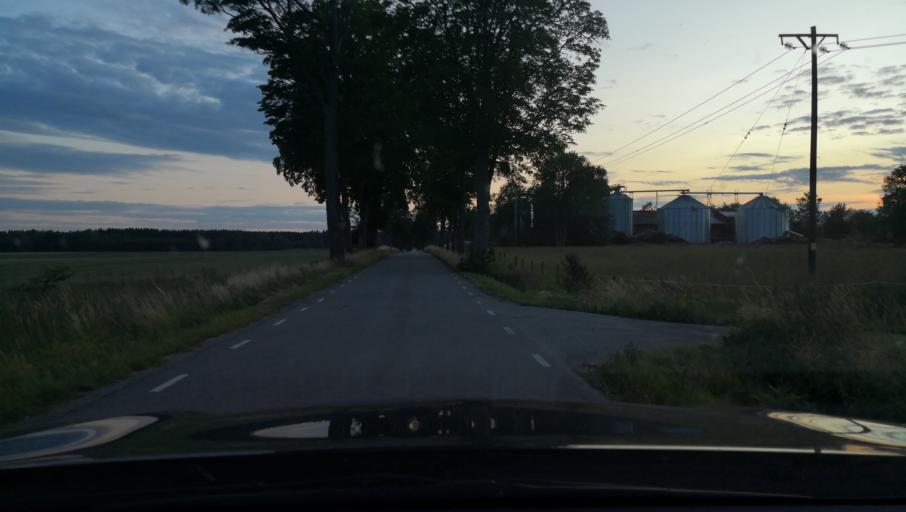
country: SE
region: Uppsala
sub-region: Osthammars Kommun
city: Bjorklinge
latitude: 60.0615
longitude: 17.5650
